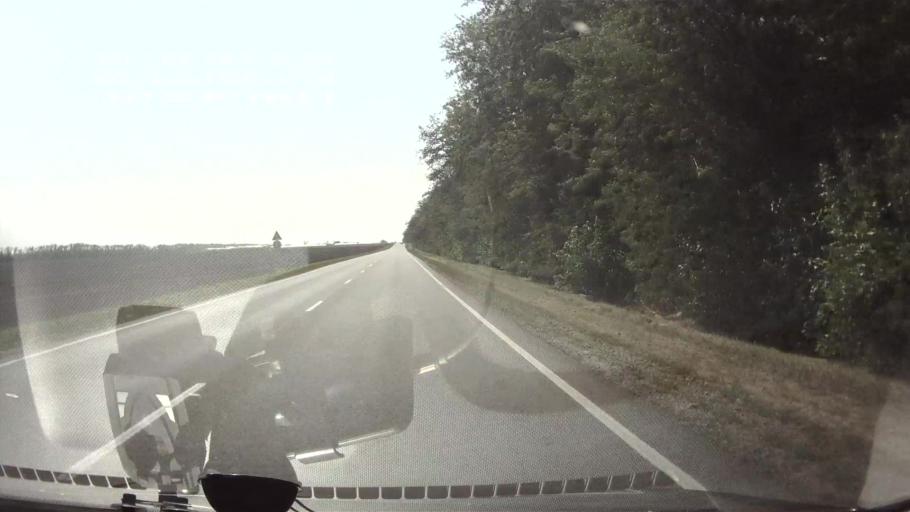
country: RU
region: Krasnodarskiy
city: Kavkazskaya
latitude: 45.4948
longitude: 40.6804
